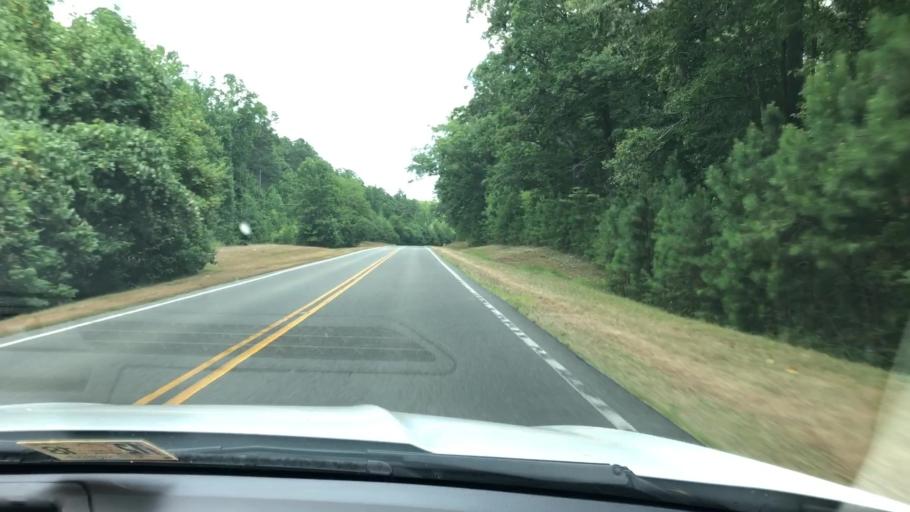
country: US
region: Virginia
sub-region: Lancaster County
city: Lancaster
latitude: 37.8273
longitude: -76.5675
